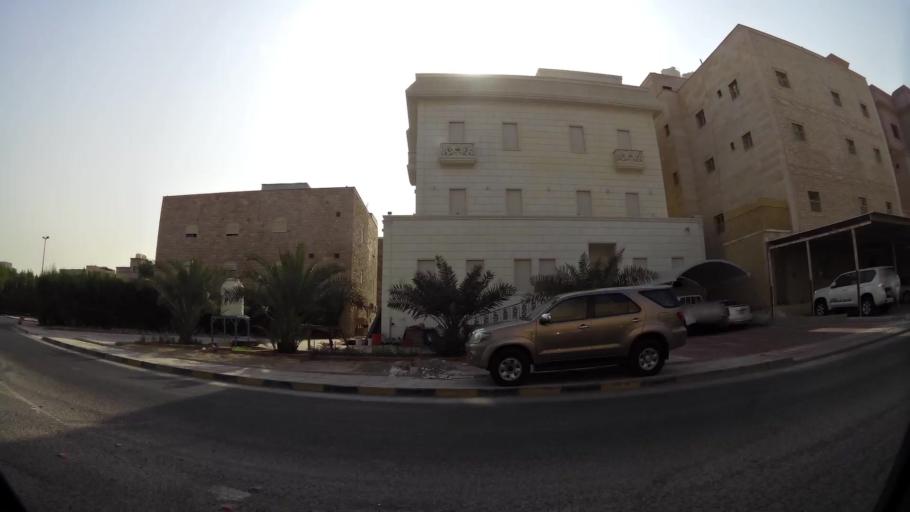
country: KW
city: Al Funaytis
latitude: 29.2203
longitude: 48.0813
